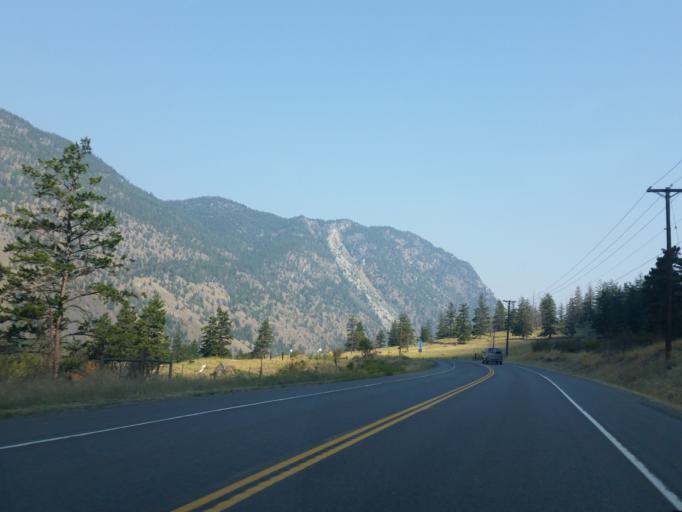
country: CA
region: British Columbia
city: Oliver
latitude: 49.2753
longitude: -120.0222
